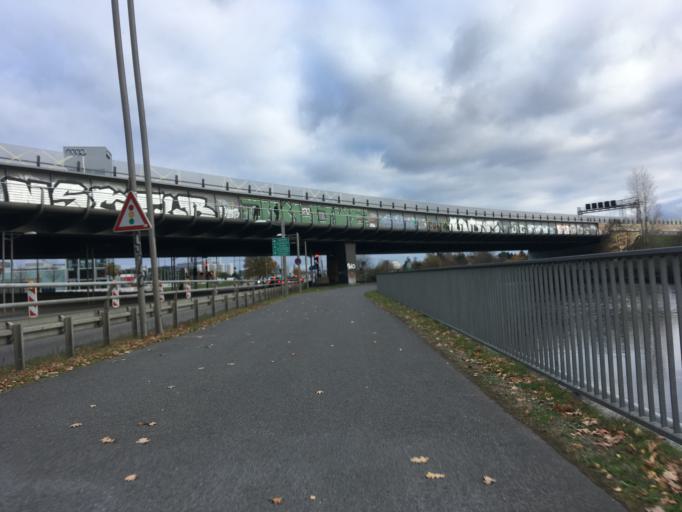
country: DE
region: Berlin
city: Johannisthal
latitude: 52.4268
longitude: 13.5183
